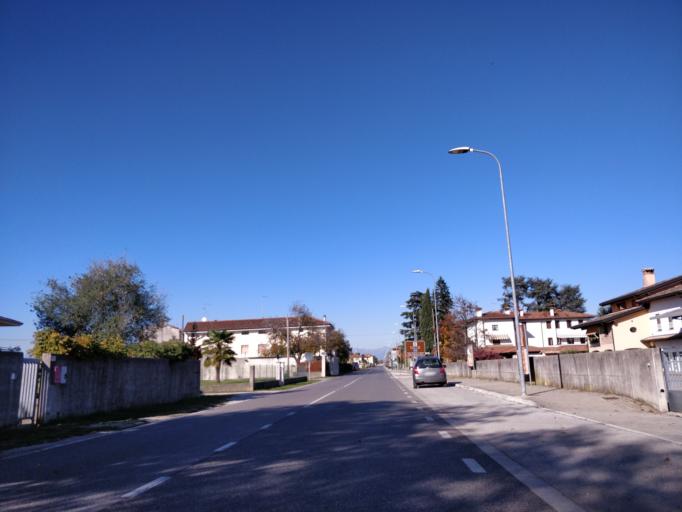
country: IT
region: Friuli Venezia Giulia
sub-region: Provincia di Udine
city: Bertiolo
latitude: 45.9442
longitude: 13.0558
